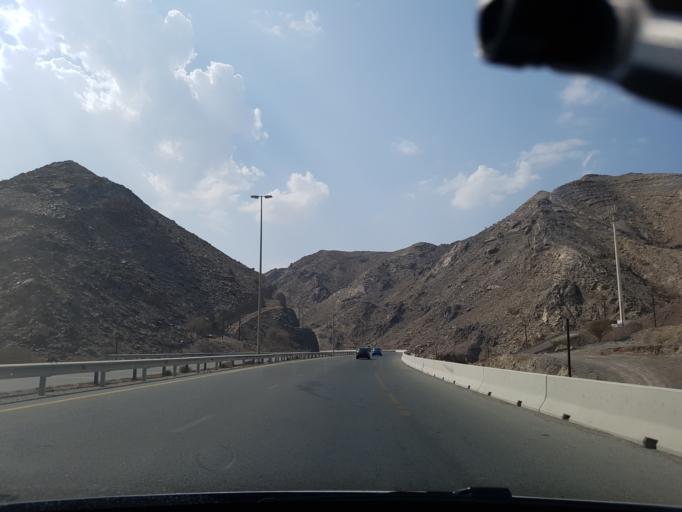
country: AE
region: Al Fujayrah
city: Dibba Al-Fujairah
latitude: 25.5338
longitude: 56.1279
